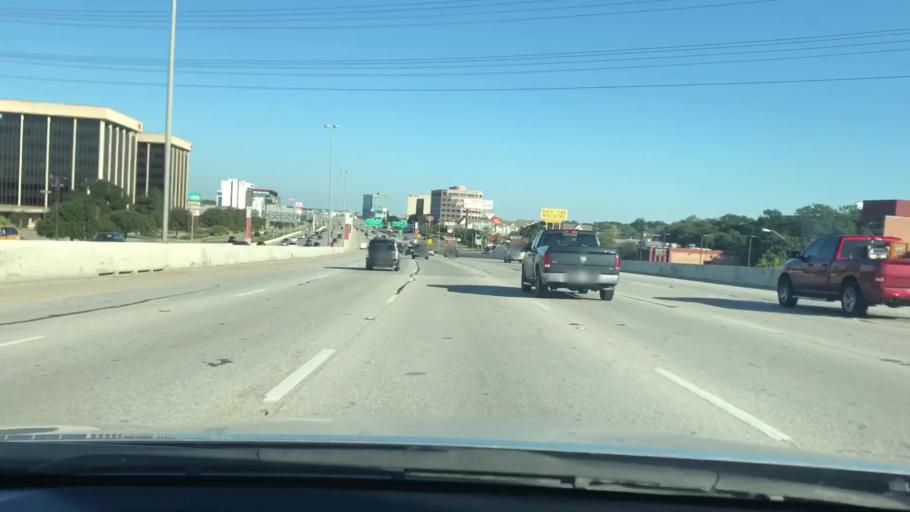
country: US
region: Texas
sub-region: Bexar County
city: Alamo Heights
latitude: 29.5167
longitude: -98.4635
